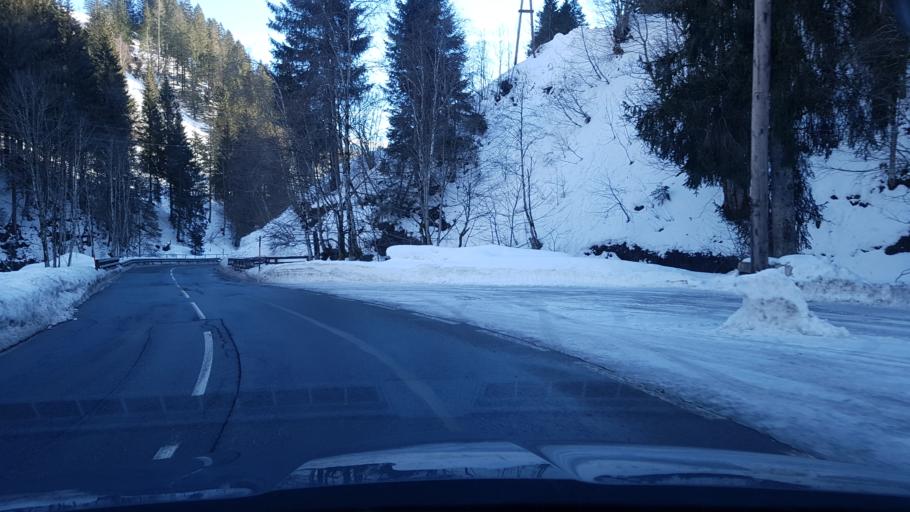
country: AT
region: Salzburg
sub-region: Politischer Bezirk Zell am See
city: Dienten am Hochkonig
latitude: 47.3451
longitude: 13.0106
